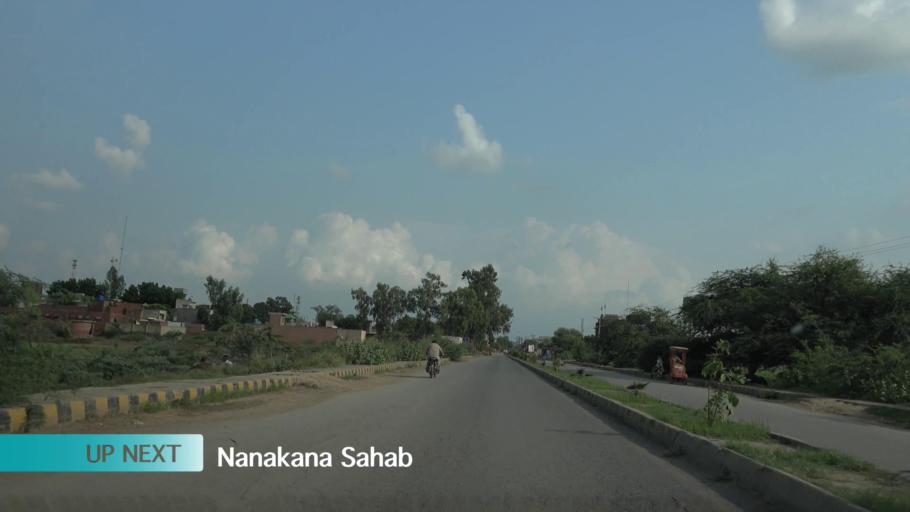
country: PK
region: Punjab
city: Nankana Sahib
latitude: 31.4530
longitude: 73.6956
